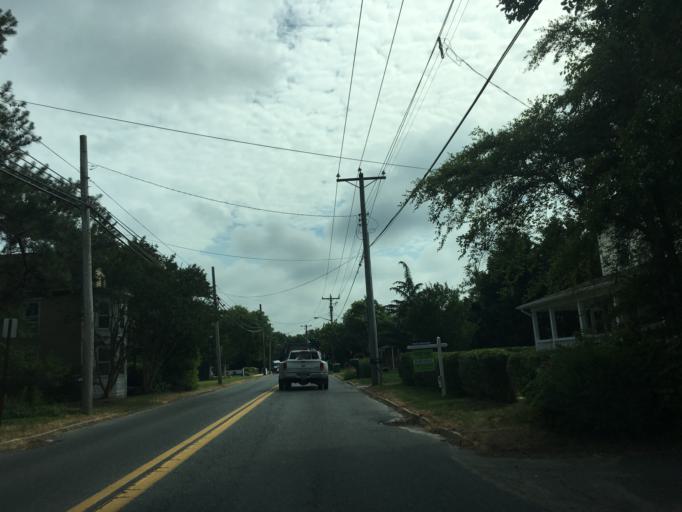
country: US
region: Delaware
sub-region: Sussex County
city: Ocean View
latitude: 38.5489
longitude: -75.0888
